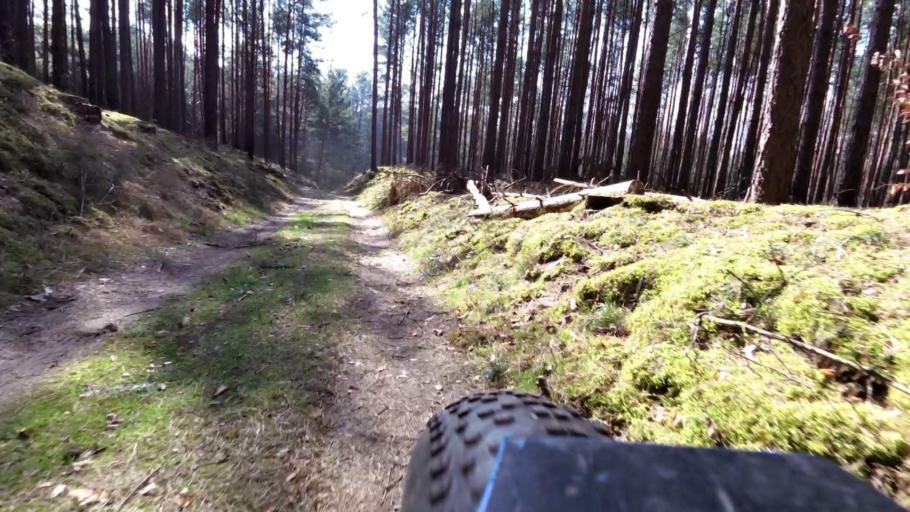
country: PL
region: Lubusz
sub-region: Powiat slubicki
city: Cybinka
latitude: 52.2090
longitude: 14.9013
